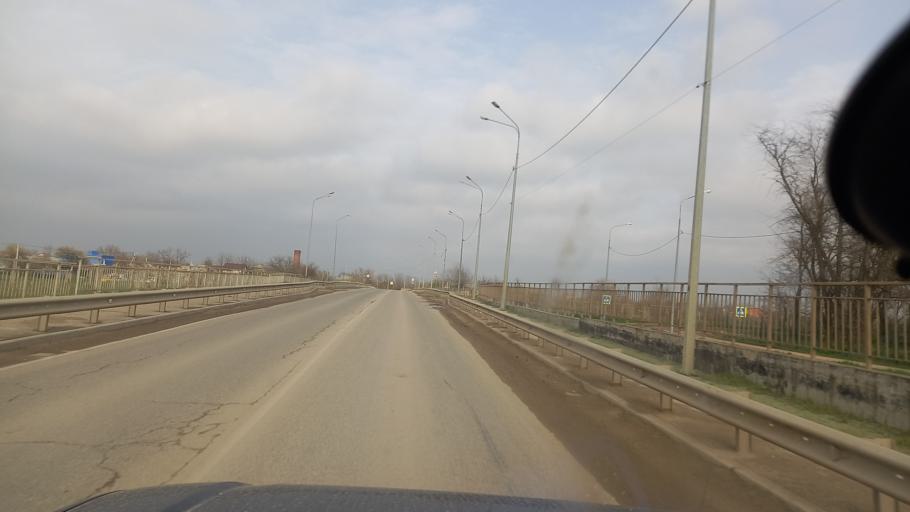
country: RU
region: Krasnodarskiy
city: Varenikovskaya
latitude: 45.1093
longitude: 37.6368
